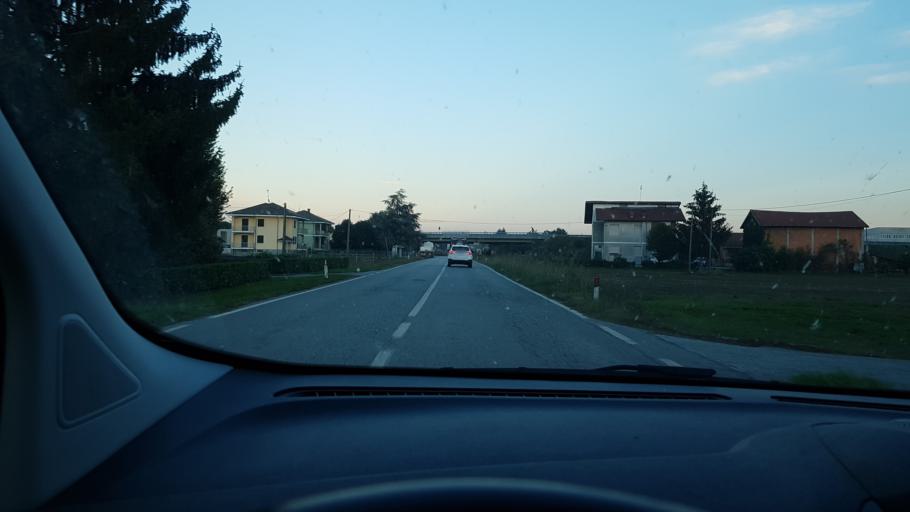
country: IT
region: Piedmont
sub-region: Provincia di Cuneo
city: Fossano
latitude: 44.5542
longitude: 7.7035
